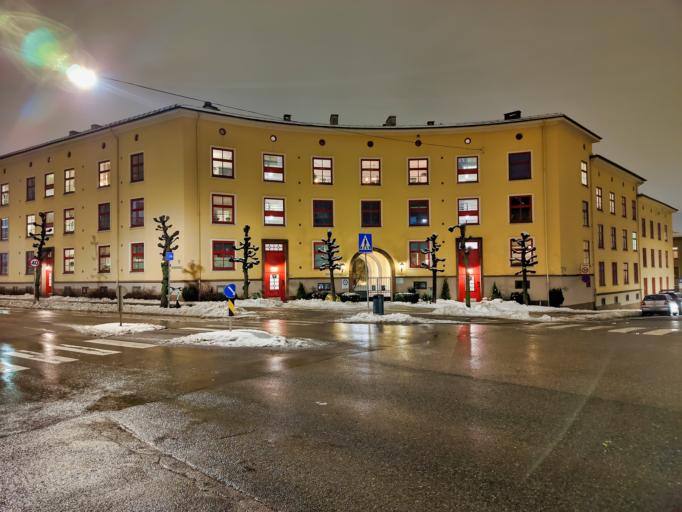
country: NO
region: Oslo
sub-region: Oslo
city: Oslo
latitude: 59.9392
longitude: 10.7748
